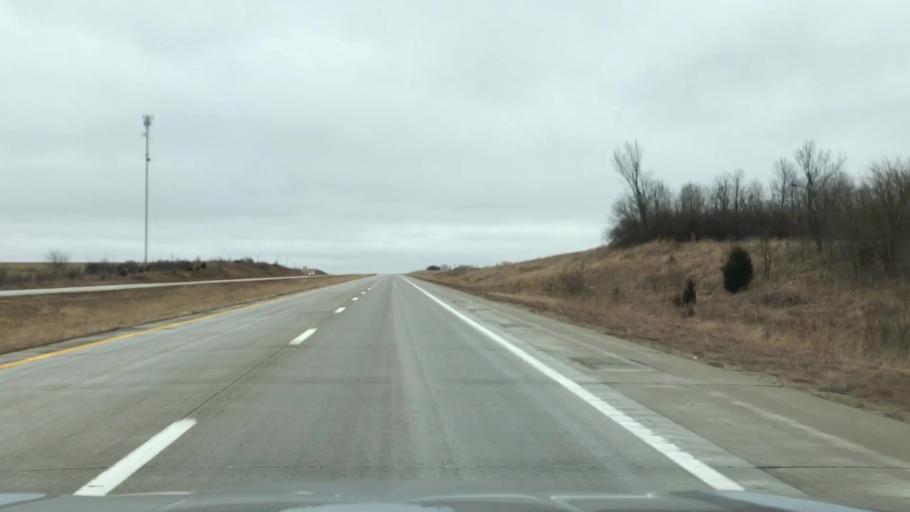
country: US
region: Missouri
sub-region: Caldwell County
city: Hamilton
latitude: 39.7348
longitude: -93.7740
